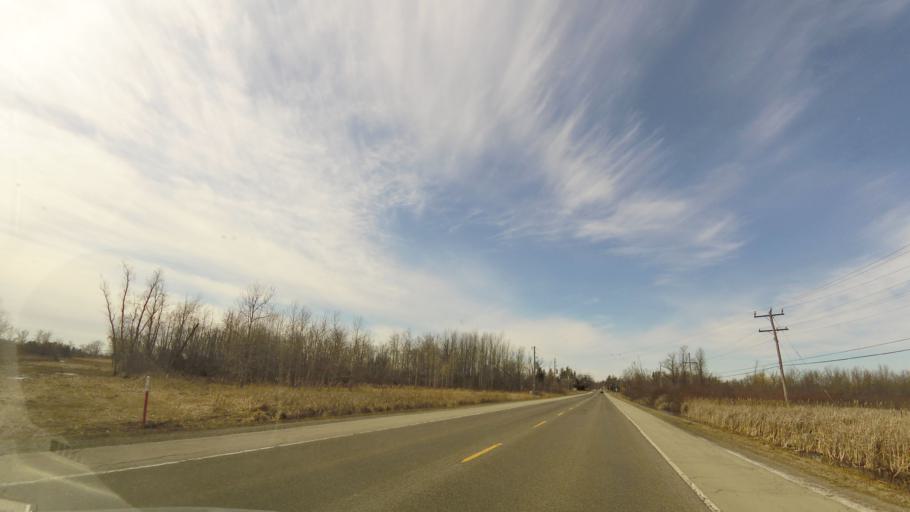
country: CA
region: Ontario
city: Burlington
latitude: 43.3685
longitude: -79.9468
